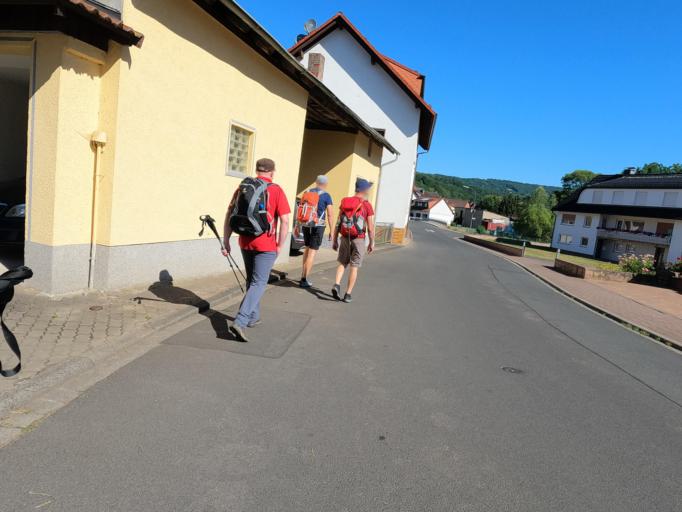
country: DE
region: Bavaria
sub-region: Regierungsbezirk Unterfranken
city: Zeitlofs
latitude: 50.3133
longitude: 9.6683
